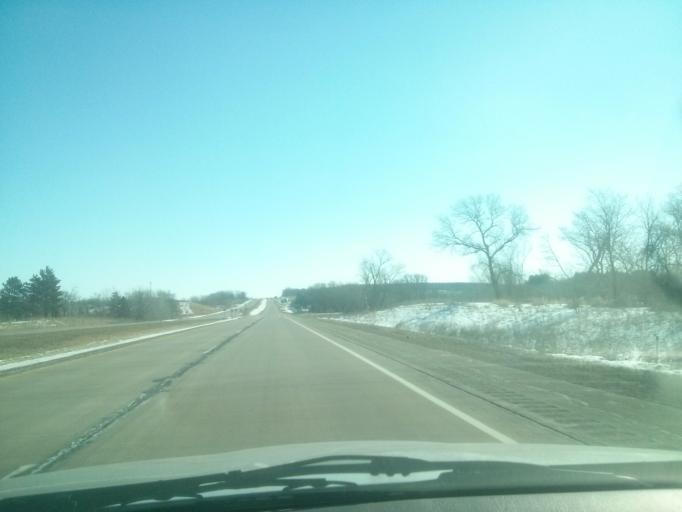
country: US
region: Wisconsin
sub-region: Saint Croix County
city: Somerset
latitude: 45.1227
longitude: -92.6141
